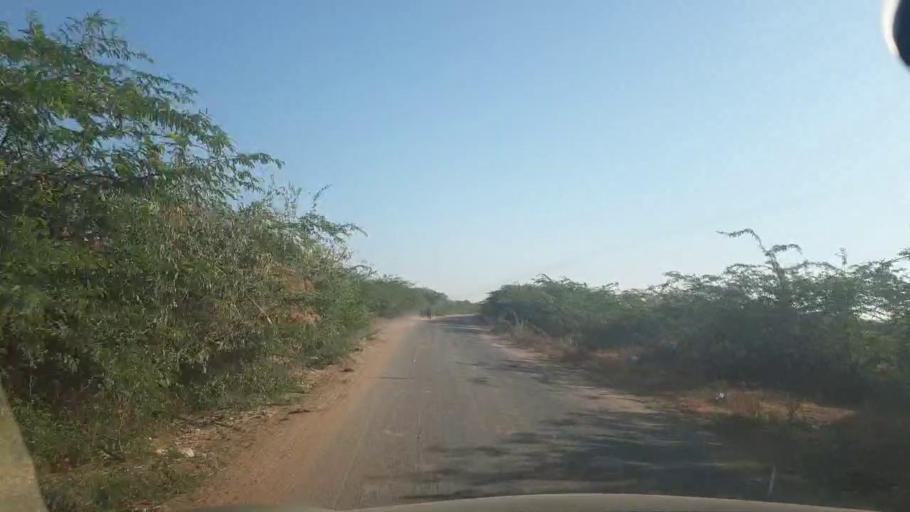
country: PK
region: Sindh
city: Malir Cantonment
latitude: 25.1127
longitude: 67.2688
